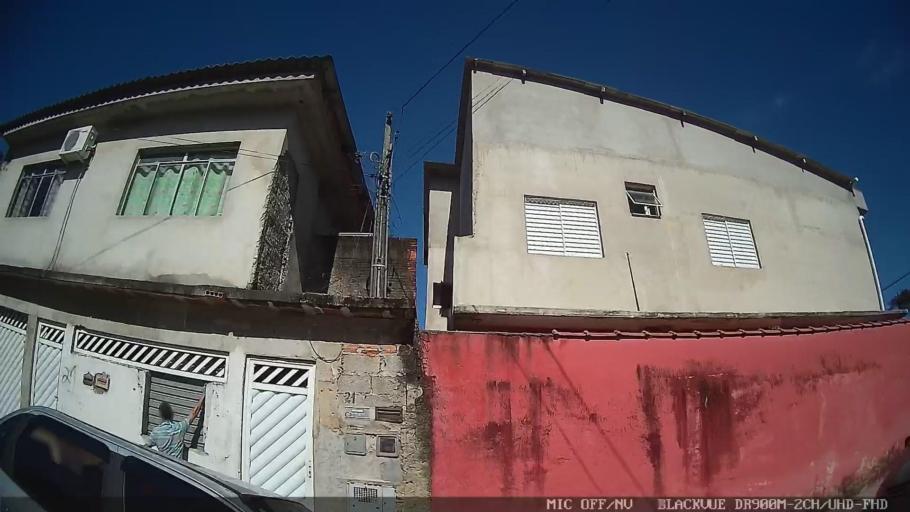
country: BR
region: Sao Paulo
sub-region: Santos
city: Santos
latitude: -23.9428
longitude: -46.2858
